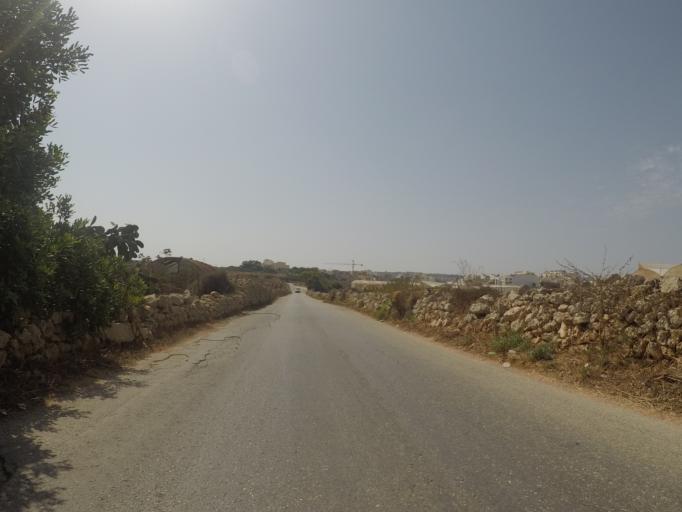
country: MT
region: L-Imgarr
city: Imgarr
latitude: 35.9261
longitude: 14.3783
